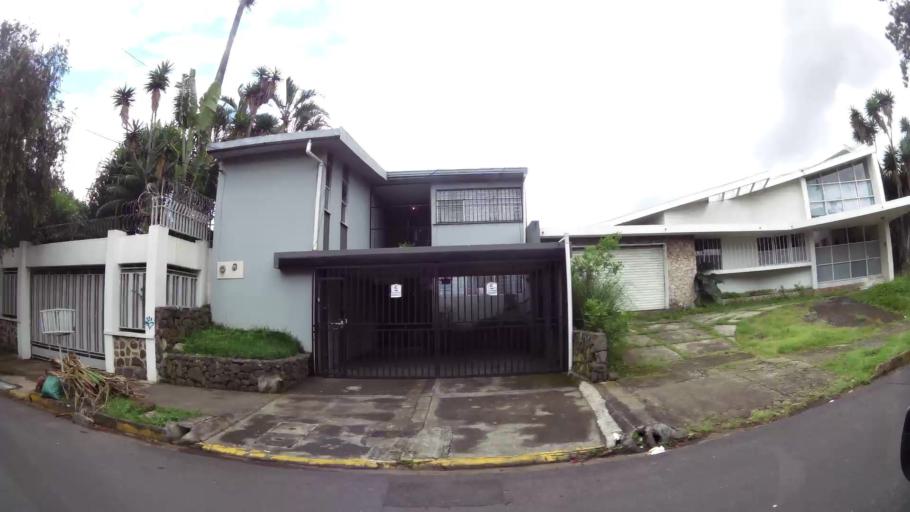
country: CR
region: San Jose
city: San Pedro
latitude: 9.9309
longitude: -84.0596
